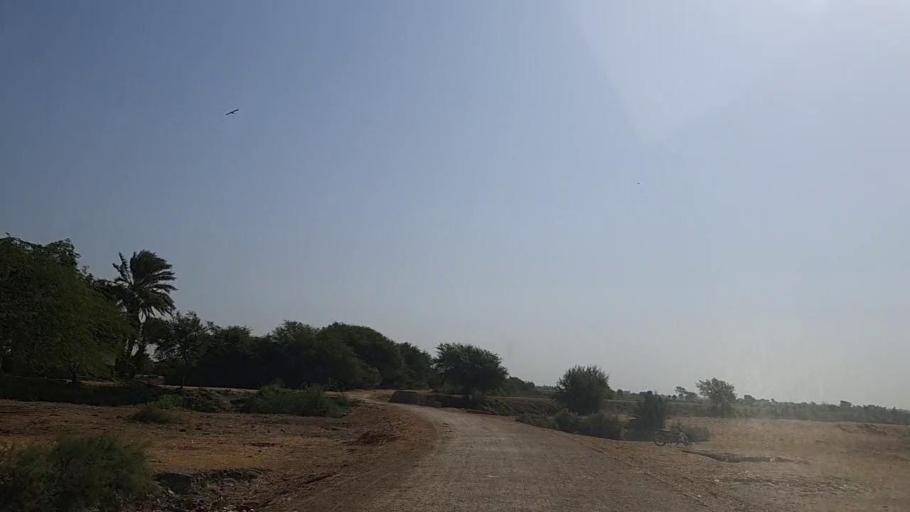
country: PK
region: Sindh
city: Daro Mehar
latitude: 24.7189
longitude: 68.1151
